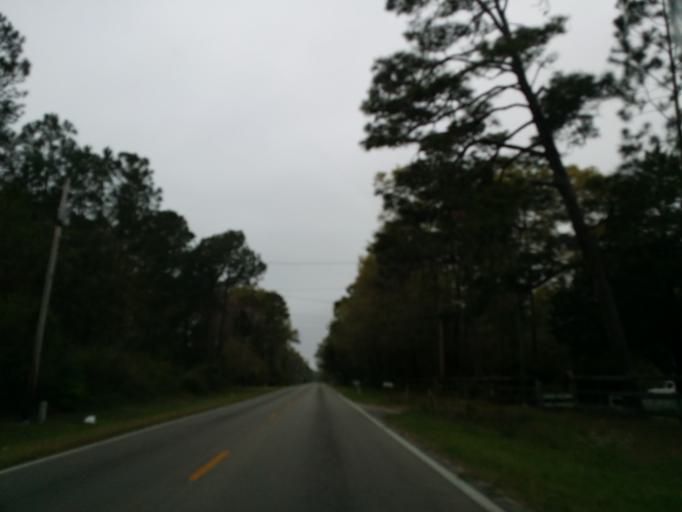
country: US
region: Florida
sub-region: Leon County
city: Woodville
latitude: 30.3215
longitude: -84.2550
